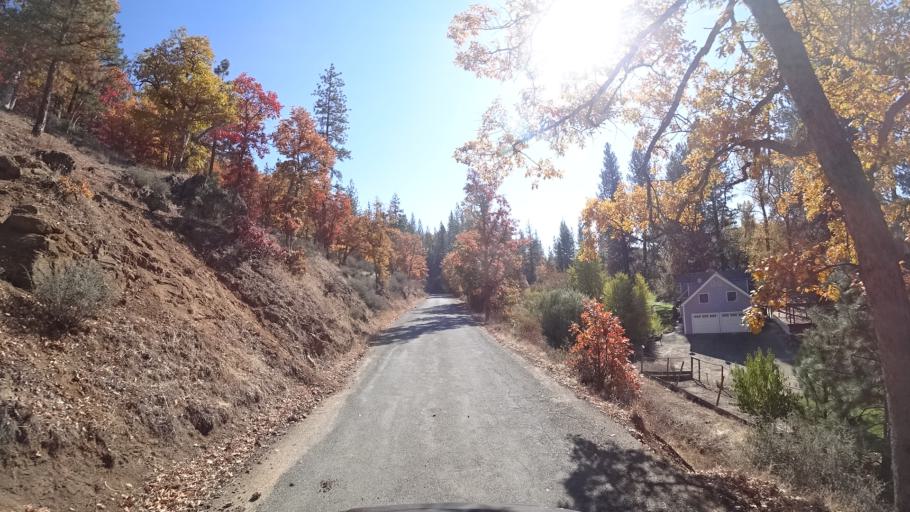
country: US
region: California
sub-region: Siskiyou County
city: Yreka
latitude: 41.6087
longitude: -122.9629
